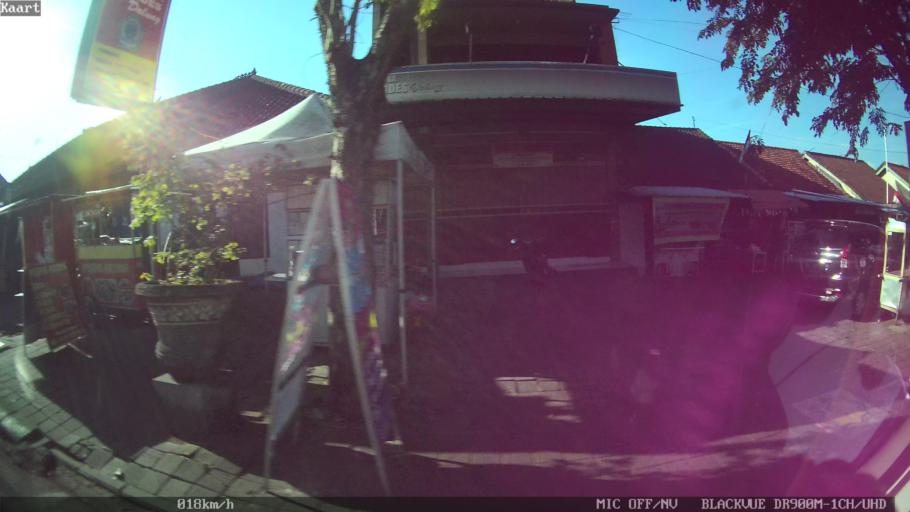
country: ID
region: Bali
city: Banjar Karangsuling
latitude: -8.6107
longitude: 115.1729
